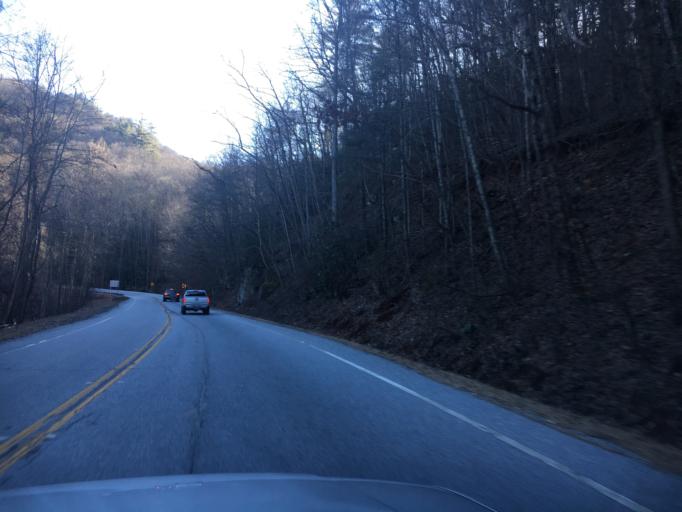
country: US
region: Georgia
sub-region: Union County
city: Blairsville
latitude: 34.7512
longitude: -83.9235
